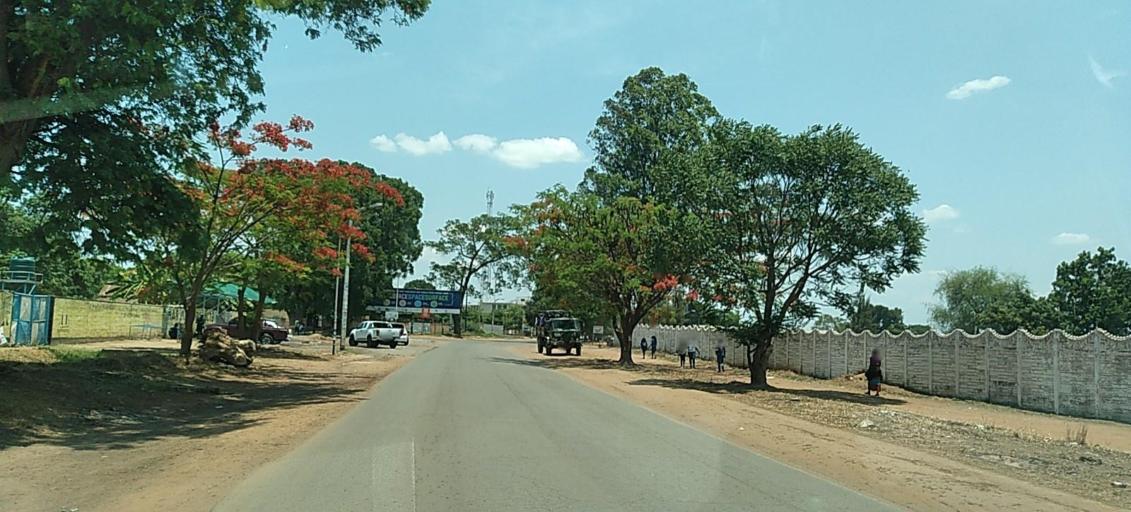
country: ZM
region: Copperbelt
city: Luanshya
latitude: -13.1382
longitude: 28.4201
